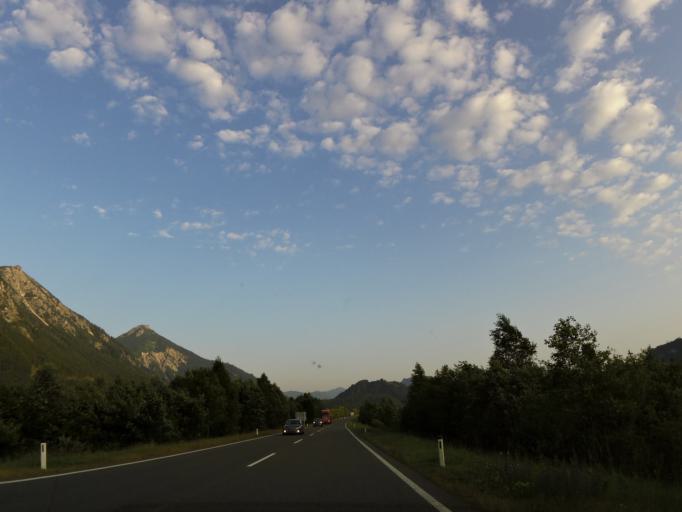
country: AT
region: Tyrol
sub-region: Politischer Bezirk Reutte
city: Pflach
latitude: 47.5273
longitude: 10.6941
